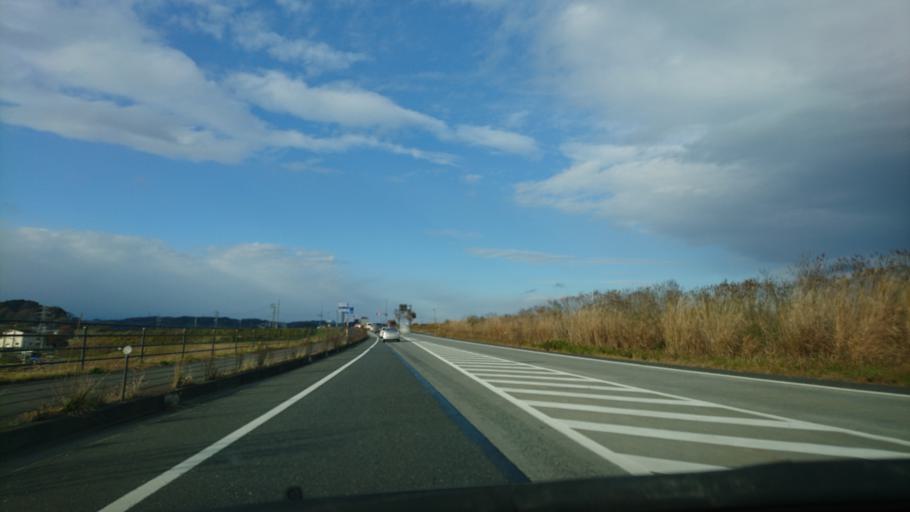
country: JP
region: Iwate
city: Ichinoseki
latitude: 38.9884
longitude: 141.1232
